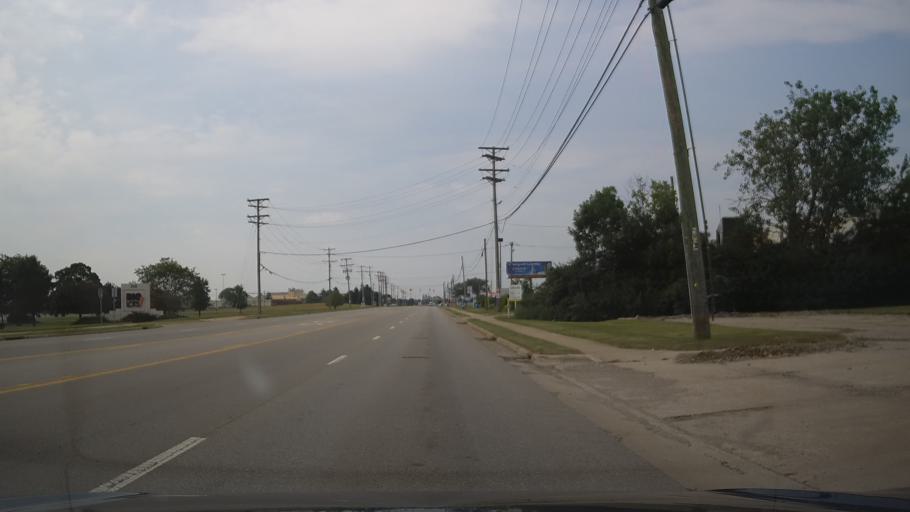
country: US
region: Ohio
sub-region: Franklin County
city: Lincoln Village
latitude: 39.9597
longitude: -83.1109
